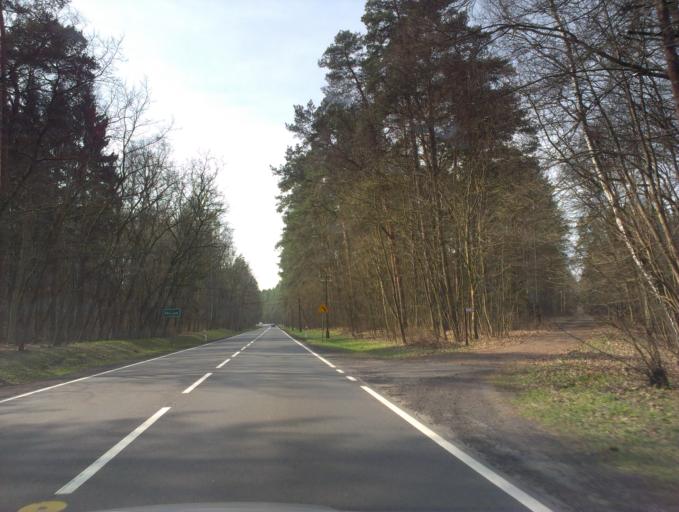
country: PL
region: Greater Poland Voivodeship
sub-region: Powiat zlotowski
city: Tarnowka
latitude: 53.3016
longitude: 16.7893
